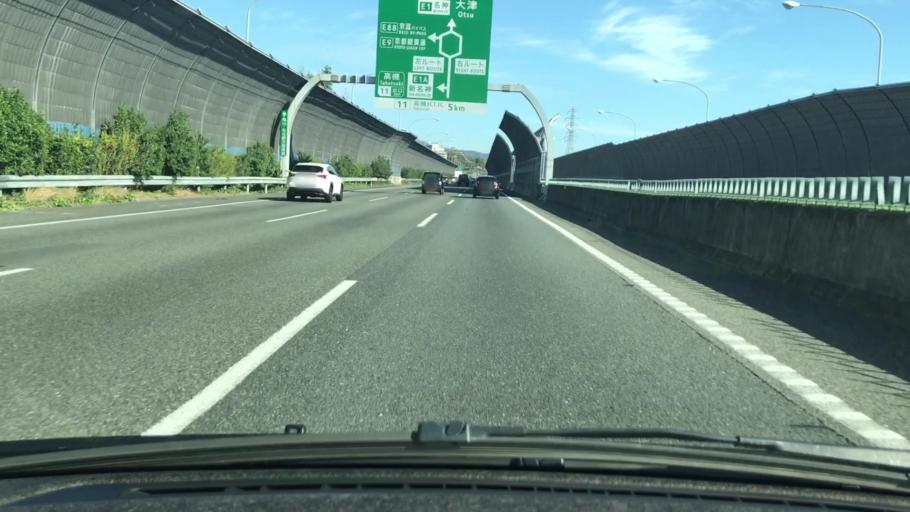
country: JP
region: Osaka
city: Ibaraki
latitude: 34.8447
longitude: 135.5748
